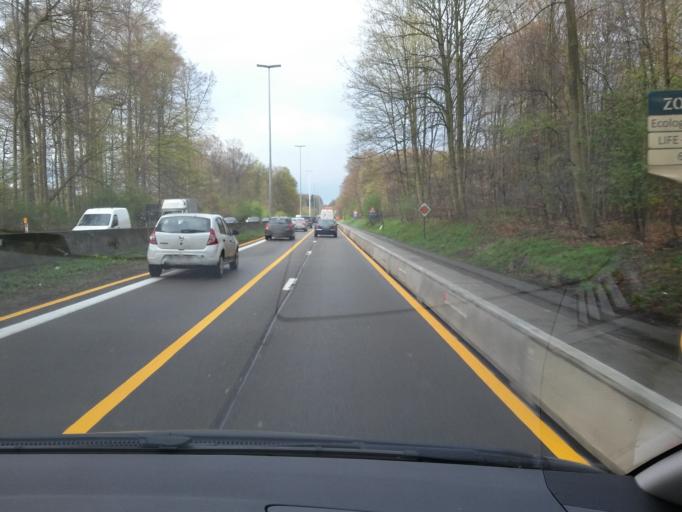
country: BE
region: Flanders
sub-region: Provincie Vlaams-Brabant
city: Hoeilaart
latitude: 50.7528
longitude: 4.4337
